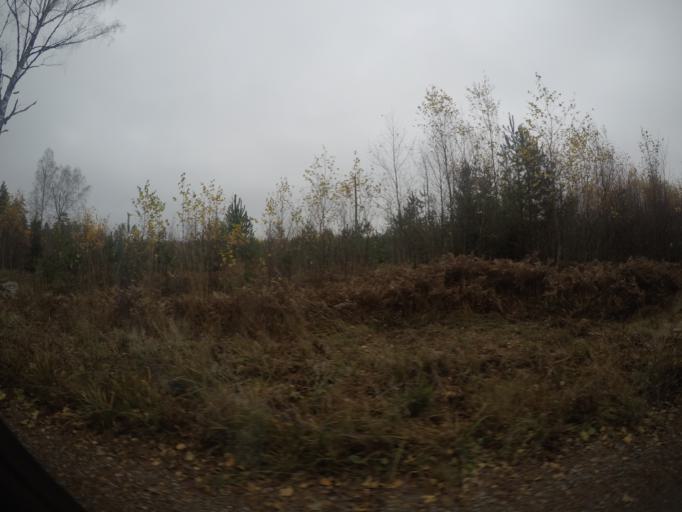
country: SE
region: Vaestmanland
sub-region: Surahammars Kommun
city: Ramnas
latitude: 59.7349
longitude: 16.1158
